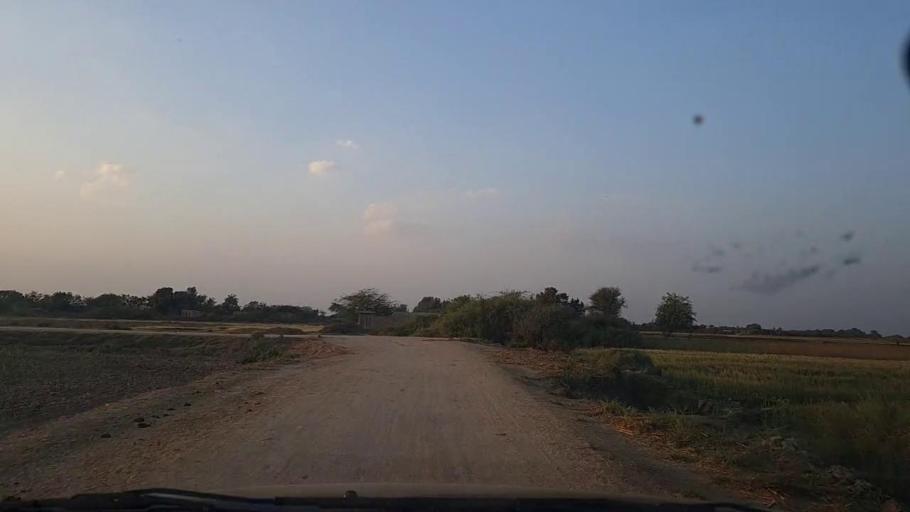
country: PK
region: Sindh
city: Daro Mehar
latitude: 24.6826
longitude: 68.1407
